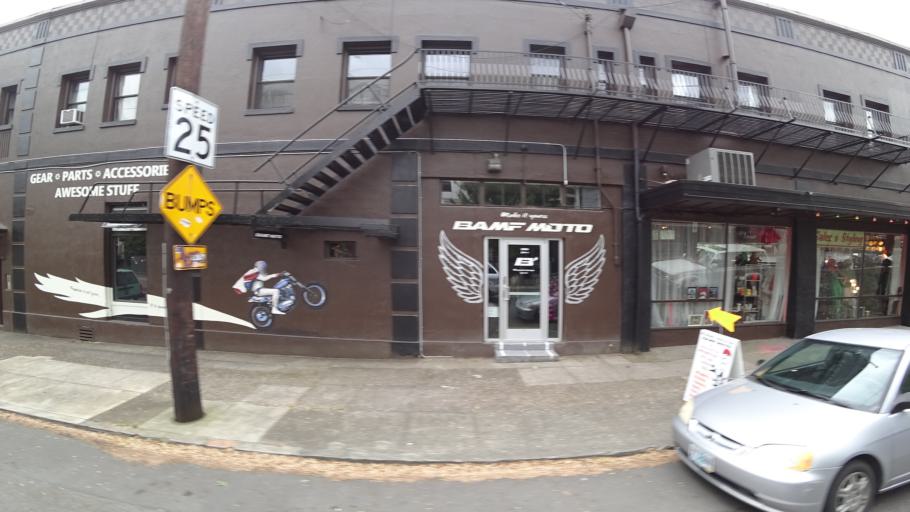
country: US
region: Oregon
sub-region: Multnomah County
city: Portland
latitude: 45.5117
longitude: -122.6452
